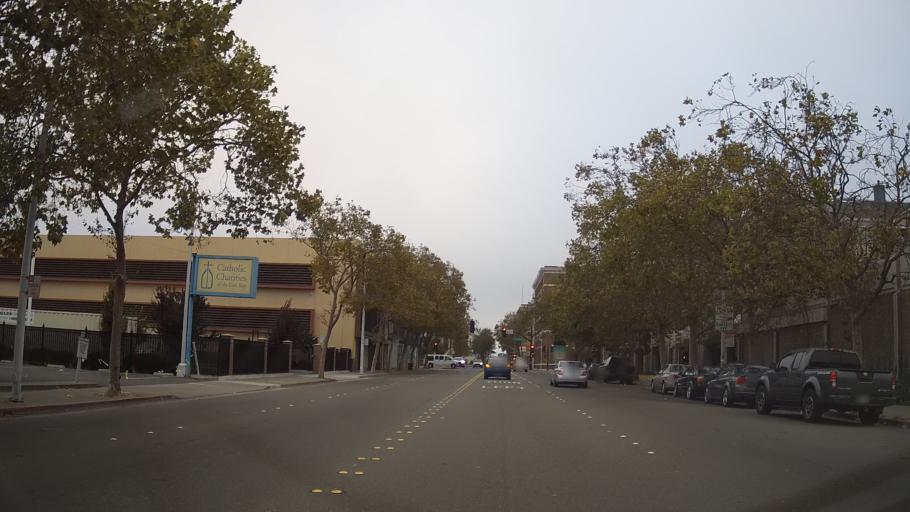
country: US
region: California
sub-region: Contra Costa County
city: Richmond
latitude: 37.9345
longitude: -122.3600
